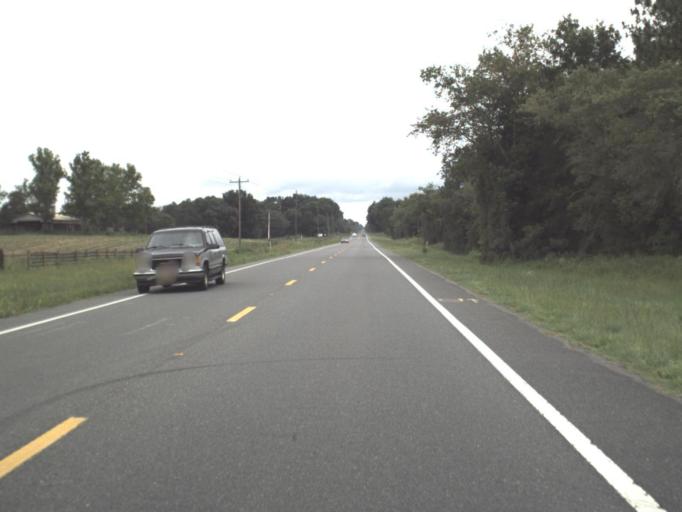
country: US
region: Florida
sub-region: Levy County
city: Williston Highlands
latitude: 29.2225
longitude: -82.4409
